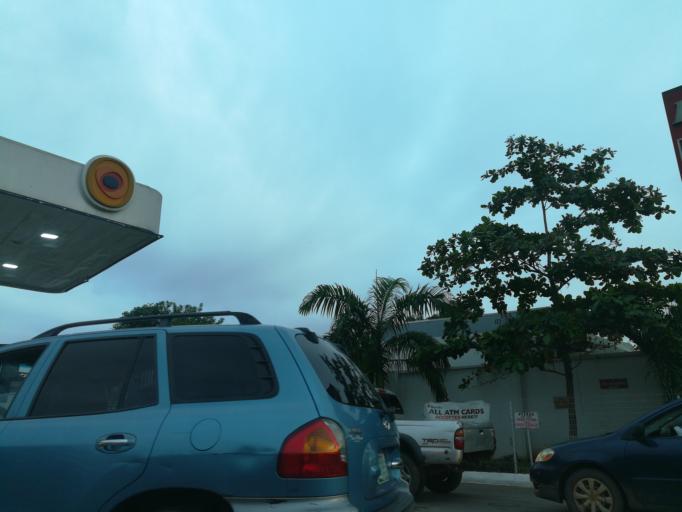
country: NG
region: Lagos
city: Ifako
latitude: 6.6379
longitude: 3.3695
